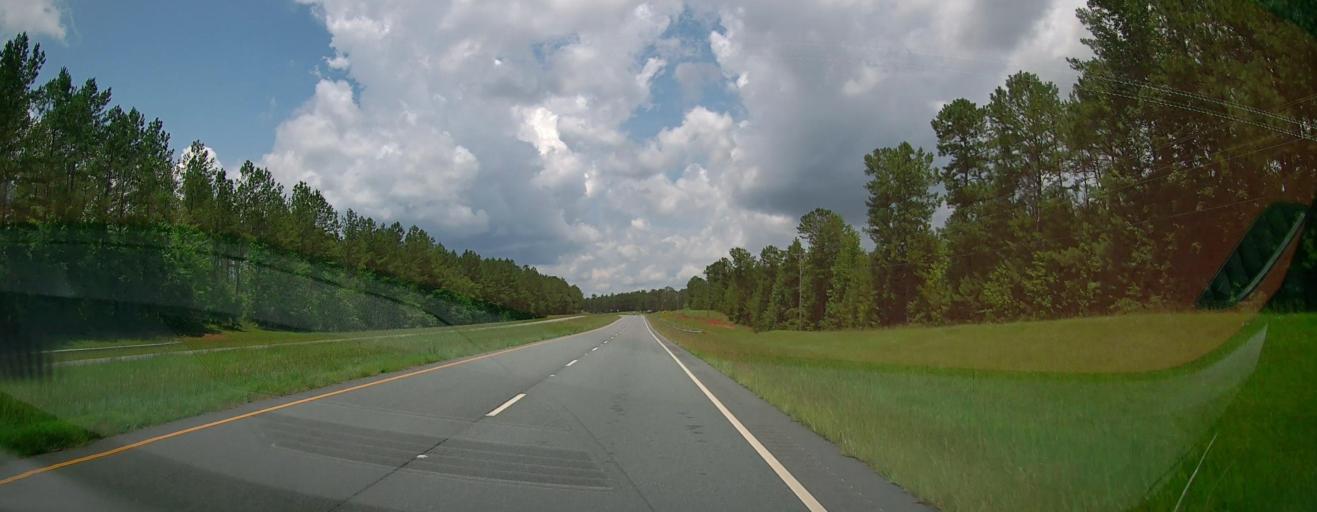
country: US
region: Georgia
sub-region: Upson County
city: Thomaston
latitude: 32.8005
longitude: -84.2739
